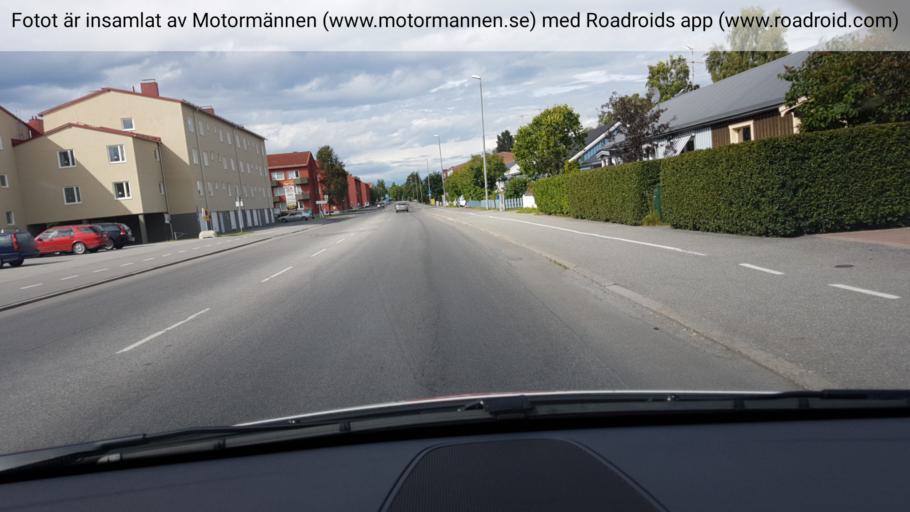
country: SE
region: Jaemtland
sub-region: OEstersunds Kommun
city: Ostersund
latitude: 63.1702
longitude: 14.6674
